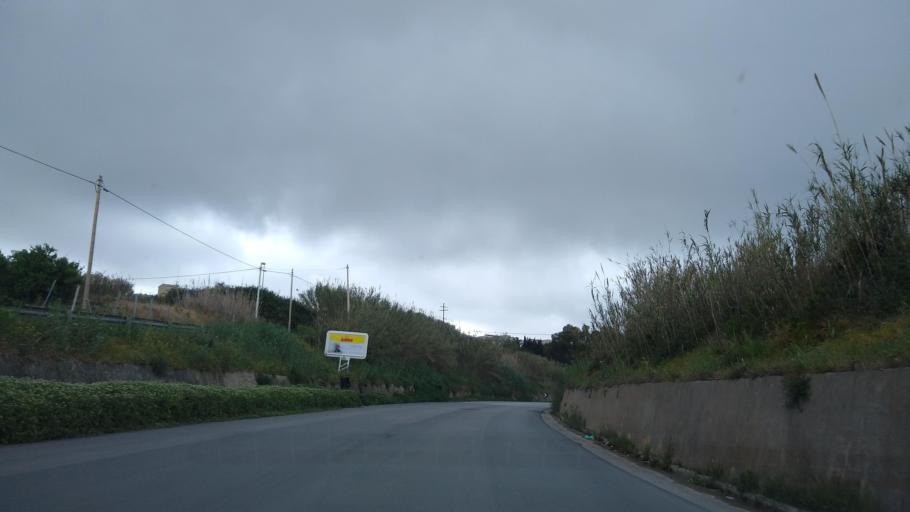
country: IT
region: Sicily
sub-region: Trapani
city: Alcamo
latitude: 37.9874
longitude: 12.9531
